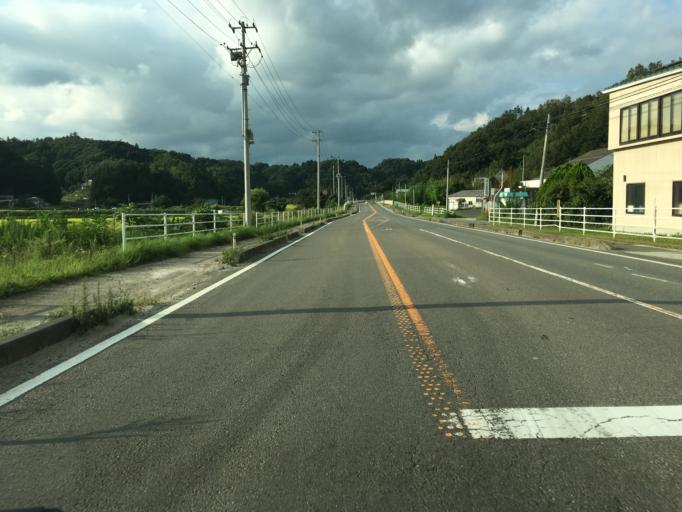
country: JP
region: Fukushima
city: Hobaramachi
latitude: 37.6977
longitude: 140.6078
